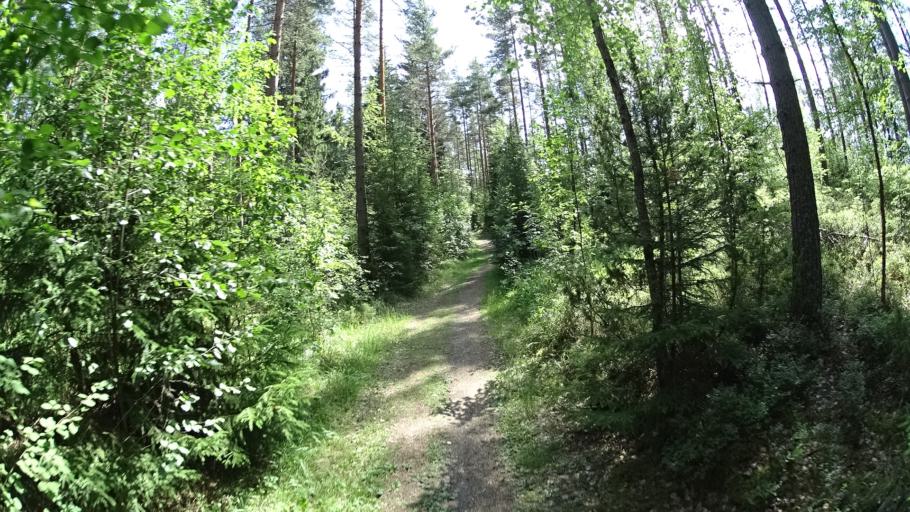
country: FI
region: Haeme
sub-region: Forssa
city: Tammela
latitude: 60.7708
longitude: 23.8676
